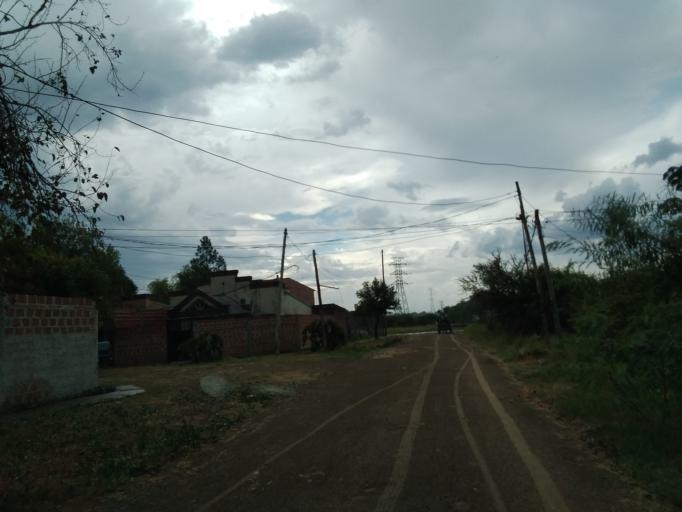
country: AR
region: Corrientes
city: Corrientes
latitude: -27.5177
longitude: -58.7883
